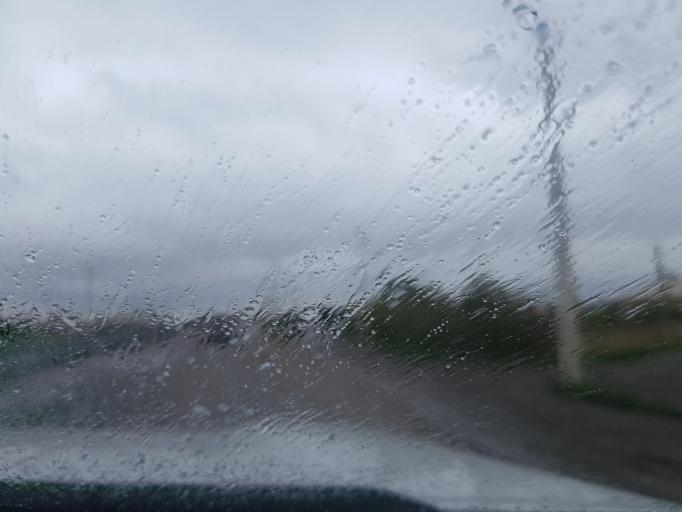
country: TM
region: Mary
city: Mary
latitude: 37.5881
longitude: 61.8825
